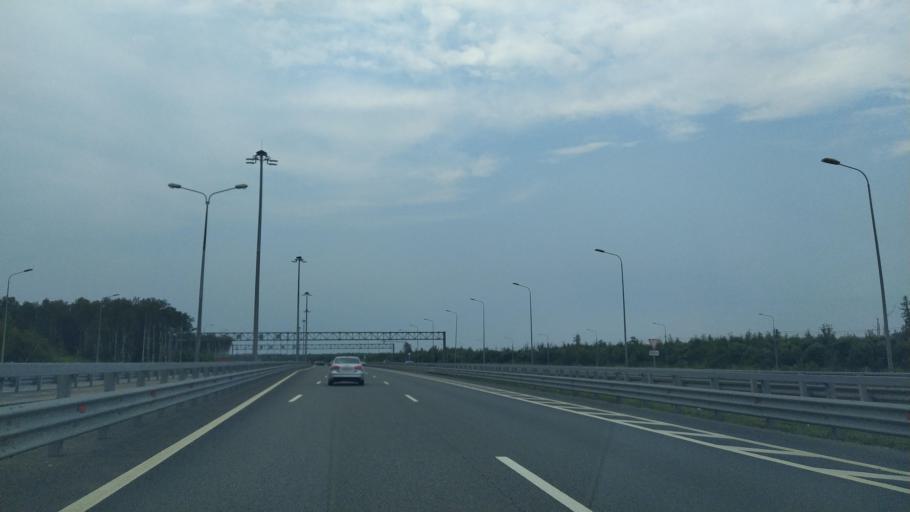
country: RU
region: St.-Petersburg
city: Pesochnyy
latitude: 60.0609
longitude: 30.1566
